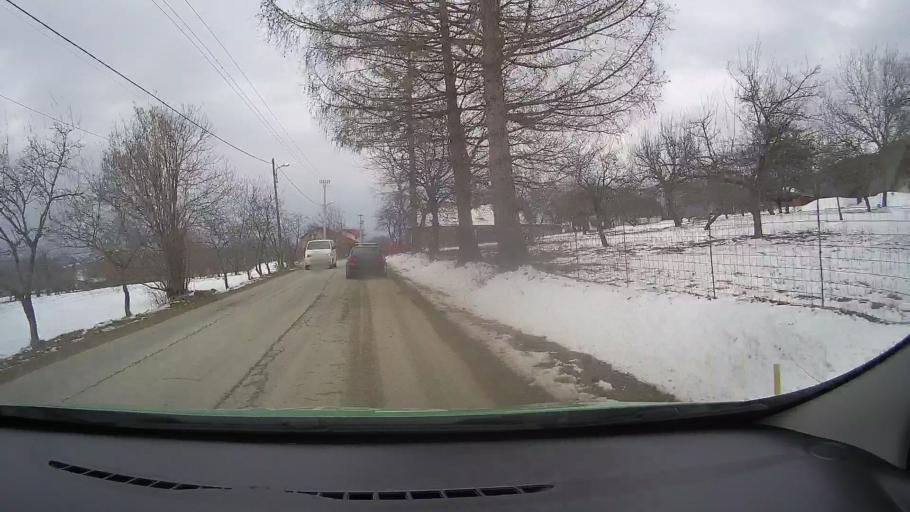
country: RO
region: Brasov
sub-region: Comuna Bran
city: Bran
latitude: 45.5374
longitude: 25.3376
